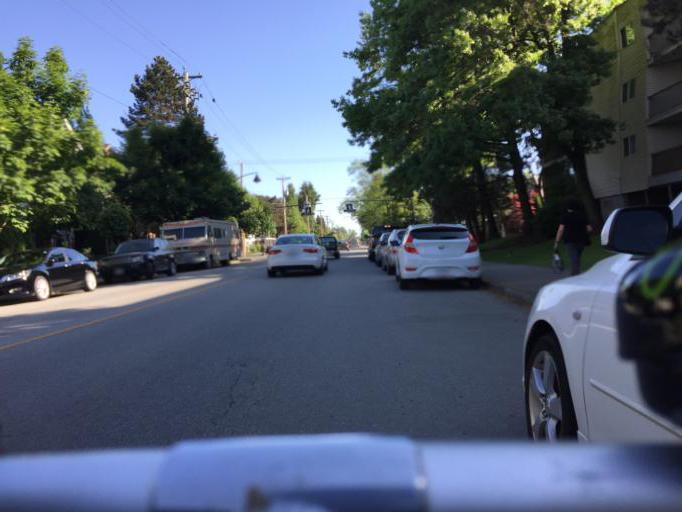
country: CA
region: British Columbia
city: Richmond
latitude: 49.1616
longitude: -123.1311
